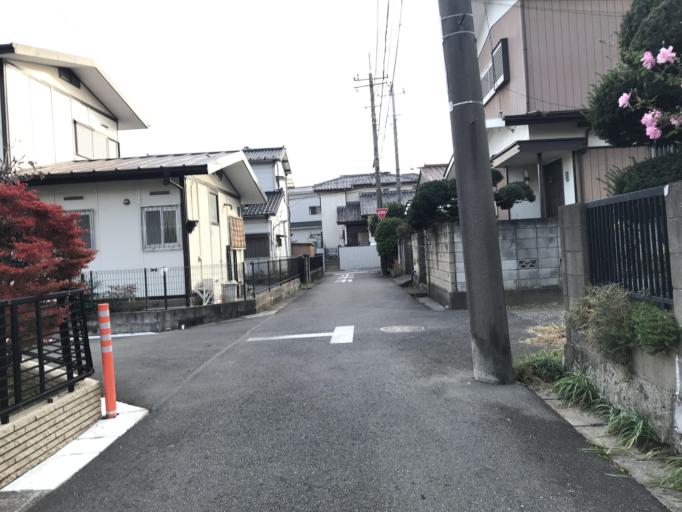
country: JP
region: Chiba
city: Shiroi
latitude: 35.7752
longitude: 140.0054
